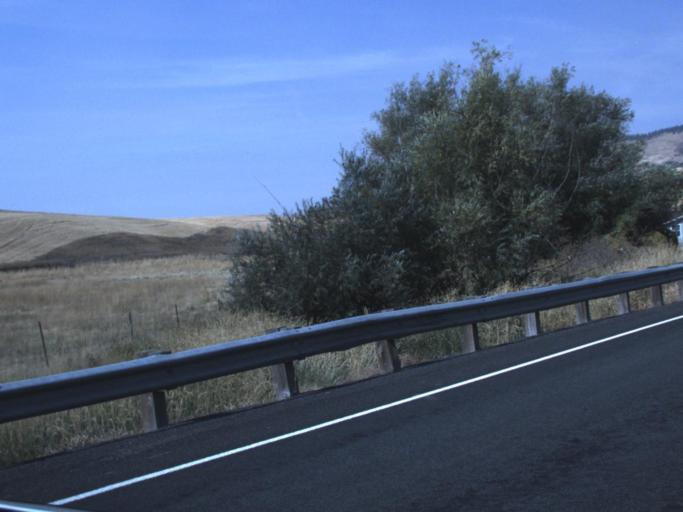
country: US
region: Washington
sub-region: Whitman County
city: Pullman
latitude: 46.8400
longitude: -117.1230
